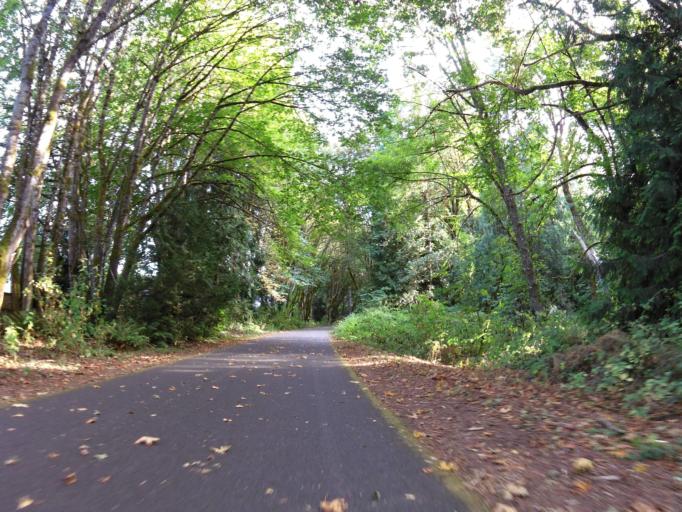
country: US
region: Washington
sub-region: Thurston County
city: Lacey
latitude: 47.0052
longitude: -122.8323
